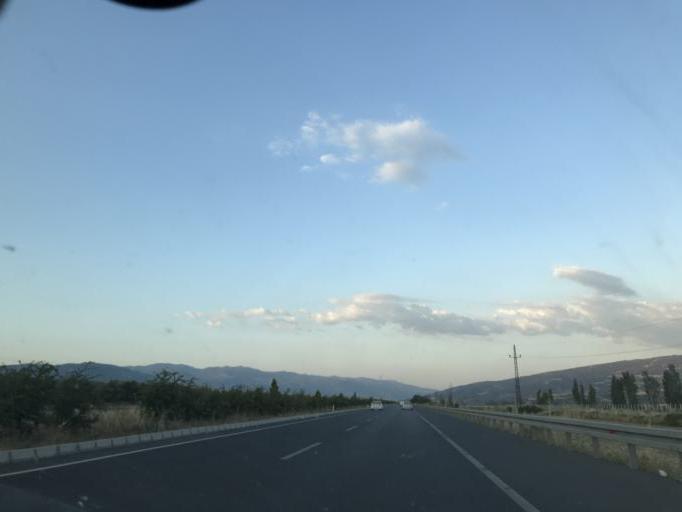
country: TR
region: Aydin
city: Horsunlu
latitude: 37.9203
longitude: 28.6351
